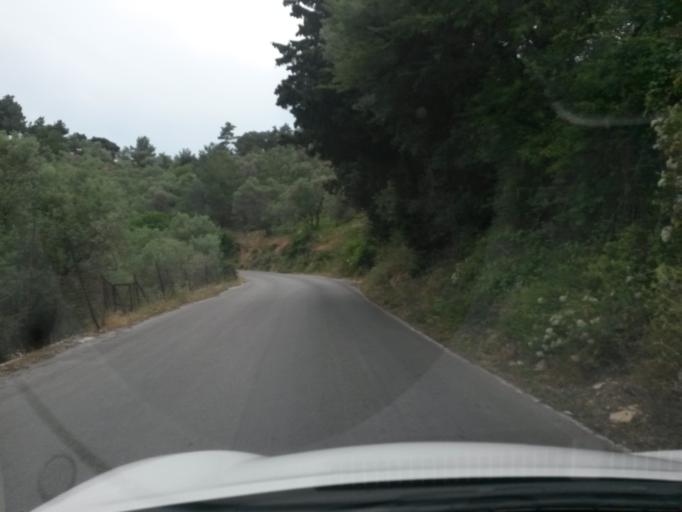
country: GR
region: North Aegean
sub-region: Nomos Lesvou
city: Skopelos
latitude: 39.0141
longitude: 26.4613
